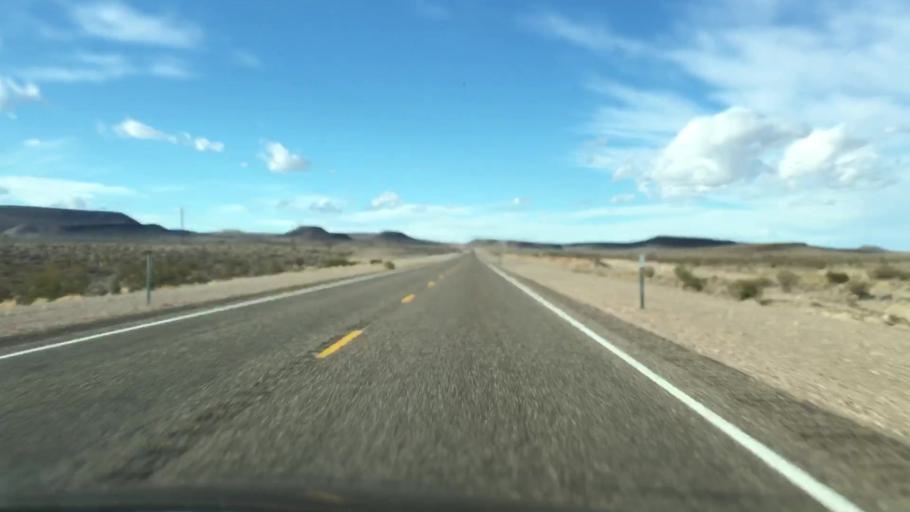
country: US
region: Nevada
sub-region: Esmeralda County
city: Goldfield
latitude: 37.3592
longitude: -117.1145
